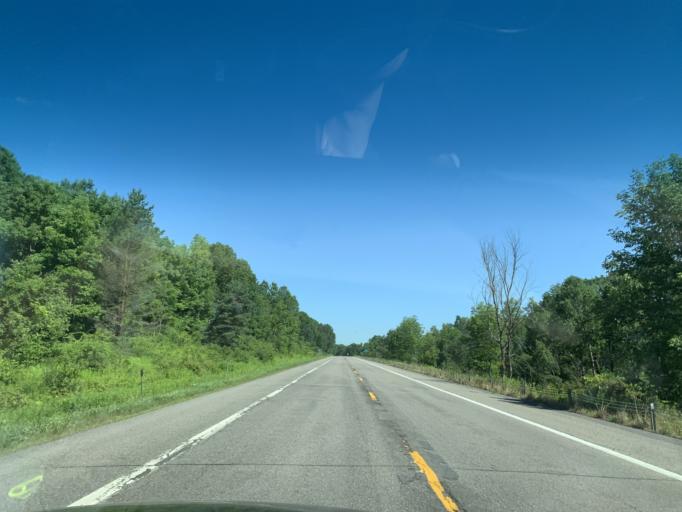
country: US
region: New York
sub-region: Chenango County
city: Norwich
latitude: 42.4666
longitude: -75.4021
